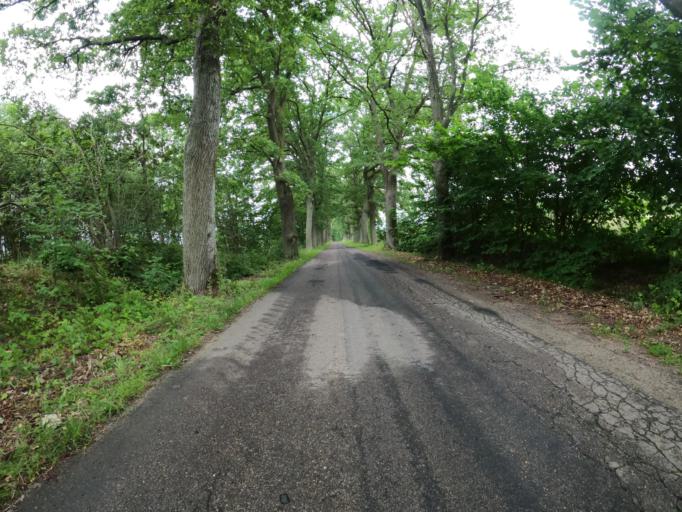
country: PL
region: West Pomeranian Voivodeship
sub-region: Powiat szczecinecki
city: Grzmiaca
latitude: 53.9279
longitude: 16.4808
